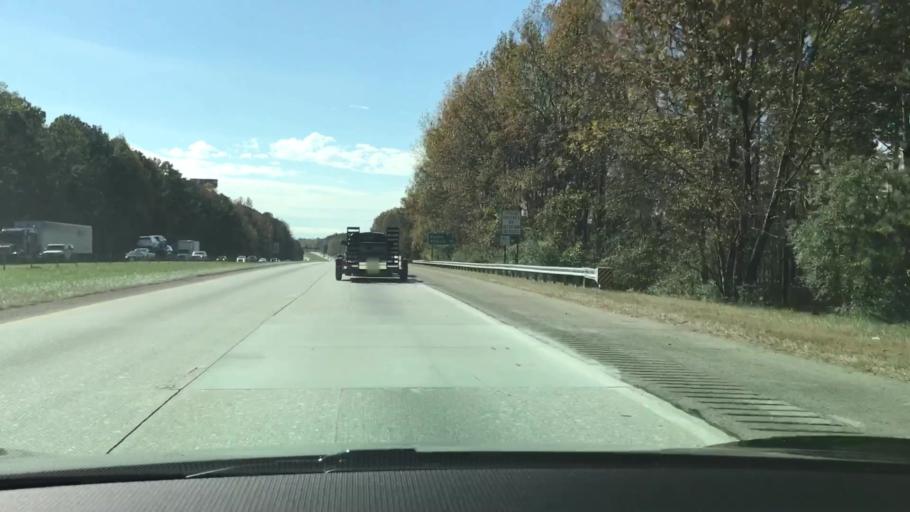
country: US
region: Georgia
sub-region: Gwinnett County
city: Buford
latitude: 34.1303
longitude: -83.9609
